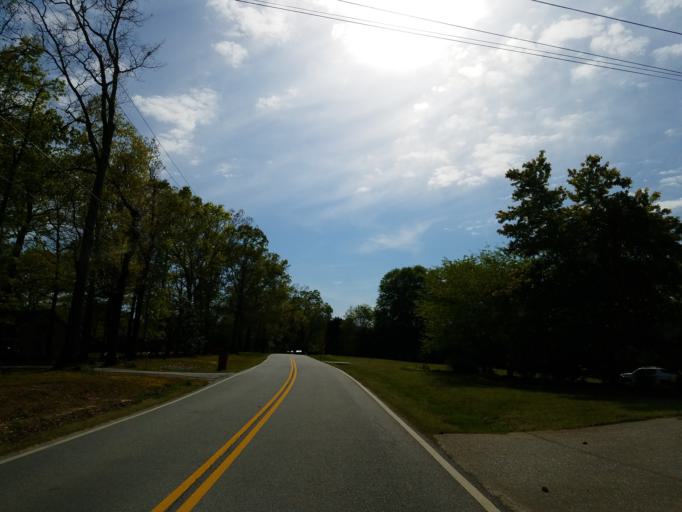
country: US
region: Georgia
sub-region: Douglas County
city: Lithia Springs
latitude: 33.7563
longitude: -84.6478
